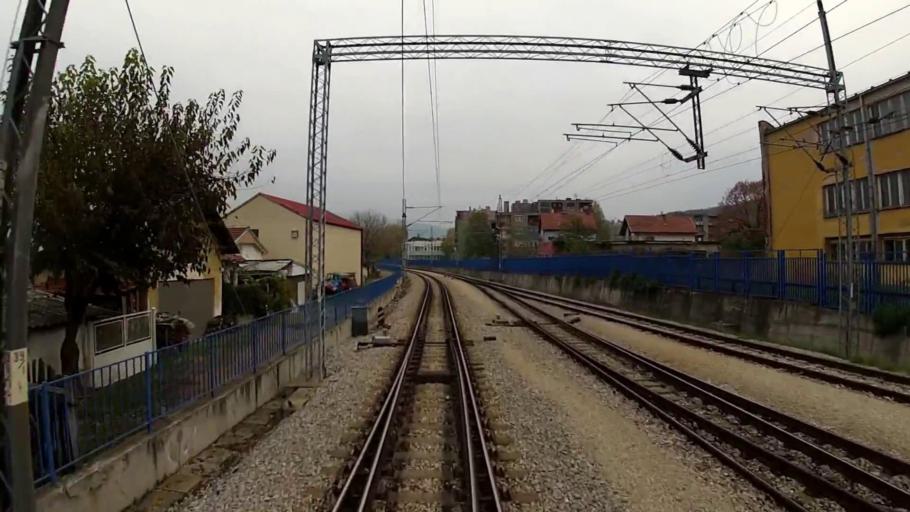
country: RS
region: Central Serbia
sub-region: Pirotski Okrug
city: Dimitrovgrad
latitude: 43.0165
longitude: 22.7783
